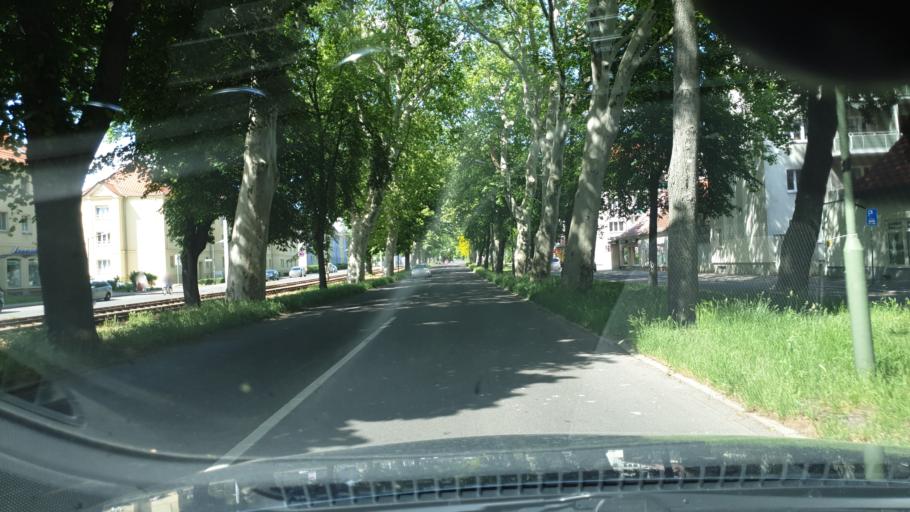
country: DE
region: Saxony-Anhalt
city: Dessau
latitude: 51.8032
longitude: 12.2410
